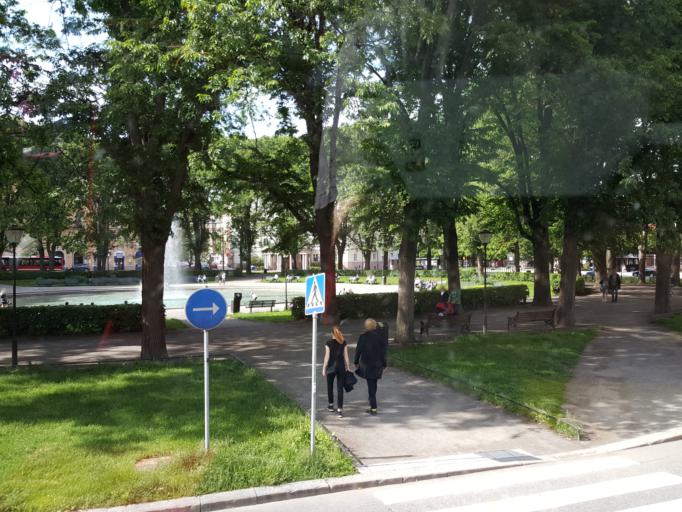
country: SE
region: Stockholm
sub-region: Stockholms Kommun
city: OEstermalm
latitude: 59.3371
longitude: 18.0907
